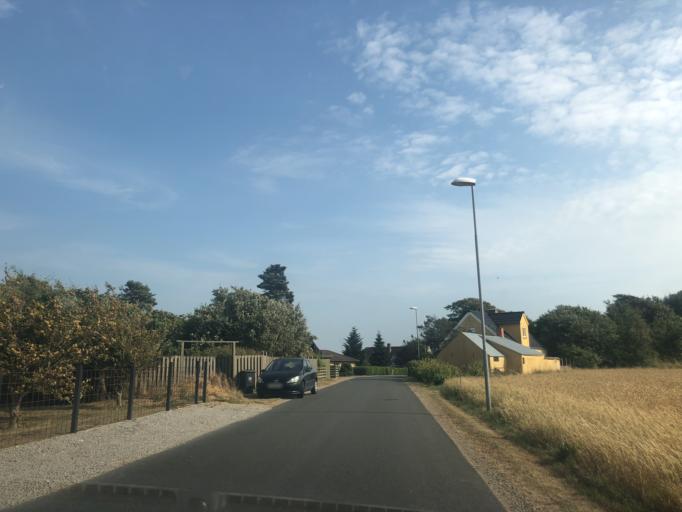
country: DK
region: North Denmark
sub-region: Morso Kommune
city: Nykobing Mors
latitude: 56.8182
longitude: 9.0220
